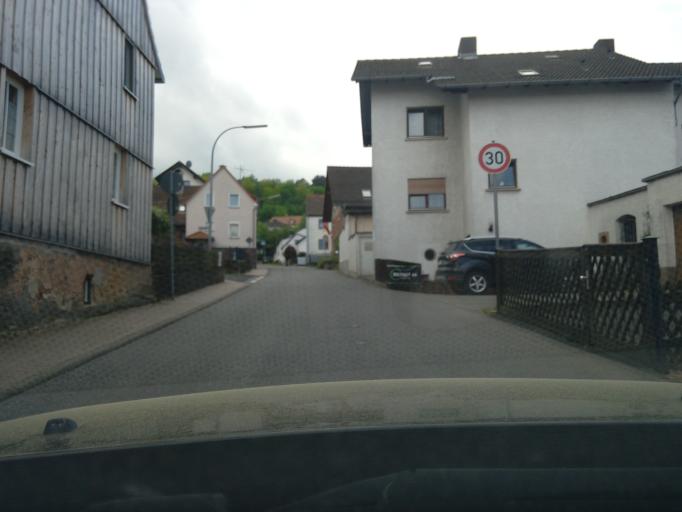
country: DE
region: Hesse
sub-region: Regierungsbezirk Darmstadt
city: Gelnhausen
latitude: 50.1798
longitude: 9.2297
